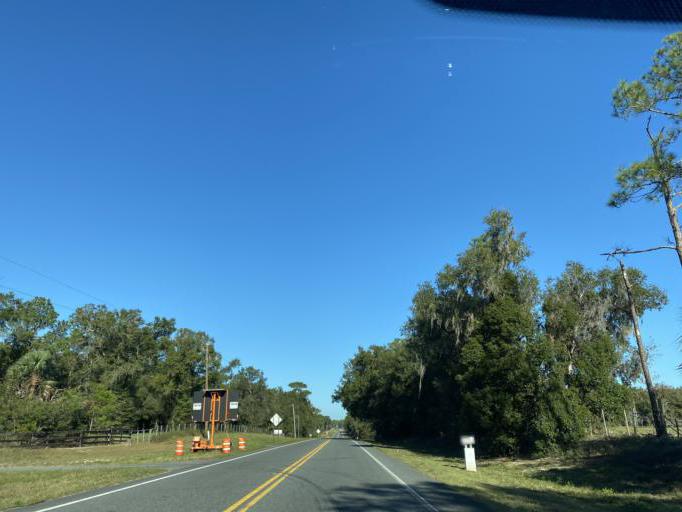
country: US
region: Florida
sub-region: Lake County
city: Mount Plymouth
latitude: 28.8395
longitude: -81.5275
